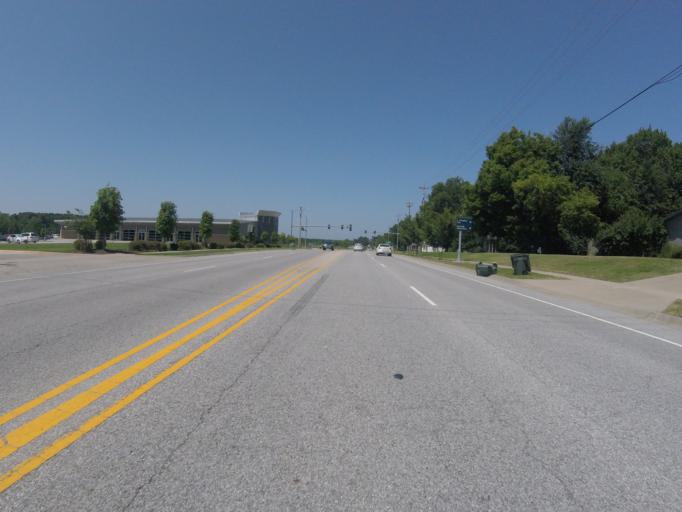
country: US
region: Arkansas
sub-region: Washington County
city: Johnson
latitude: 36.0929
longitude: -94.2071
